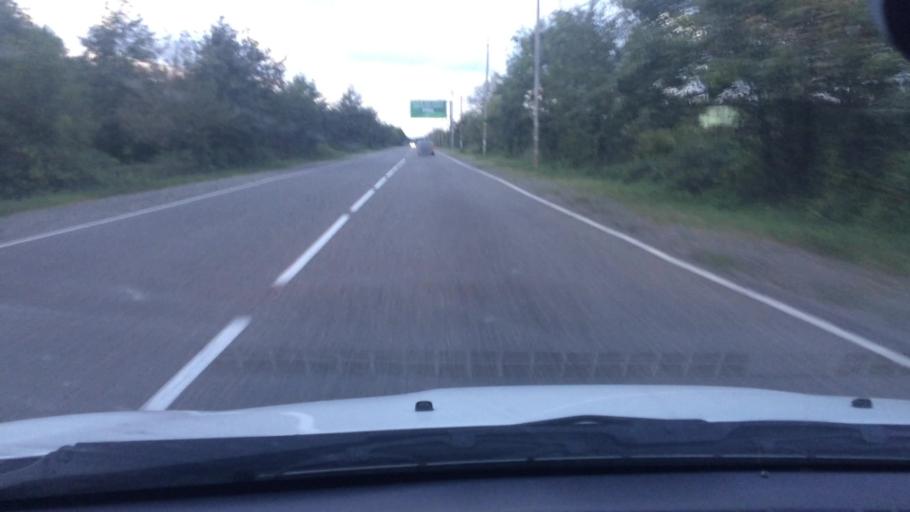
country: GE
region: Guria
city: Urek'i
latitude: 41.9326
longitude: 41.7724
